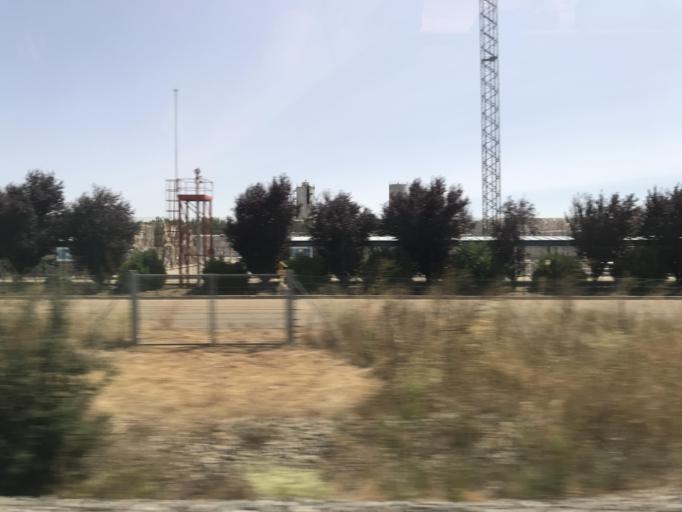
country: ES
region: Castille and Leon
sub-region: Provincia de Palencia
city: Duenas
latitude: 41.8395
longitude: -4.5605
